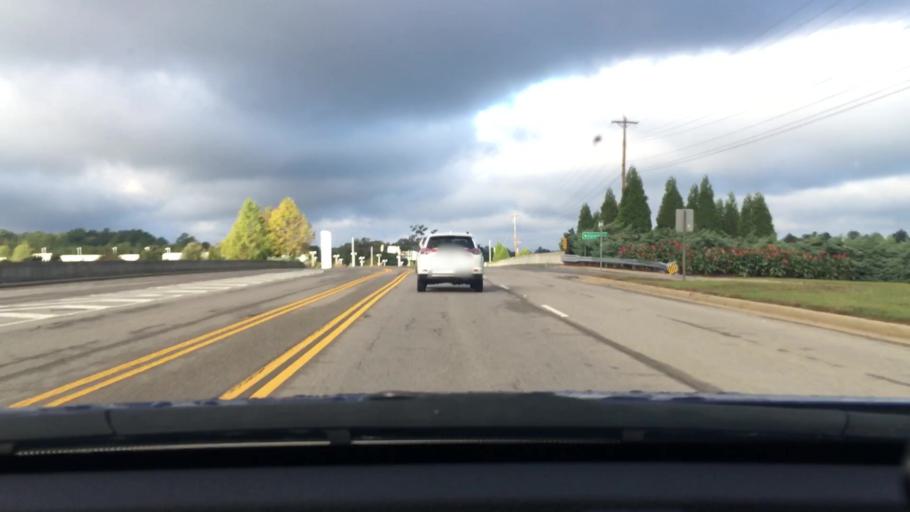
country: US
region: South Carolina
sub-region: Lexington County
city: Irmo
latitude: 34.0992
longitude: -81.1736
